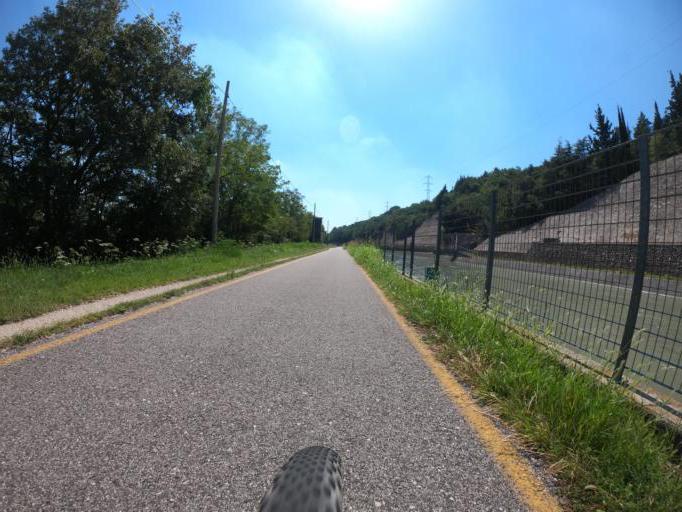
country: IT
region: Veneto
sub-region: Provincia di Verona
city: Pastrengo
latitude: 45.5168
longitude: 10.7963
